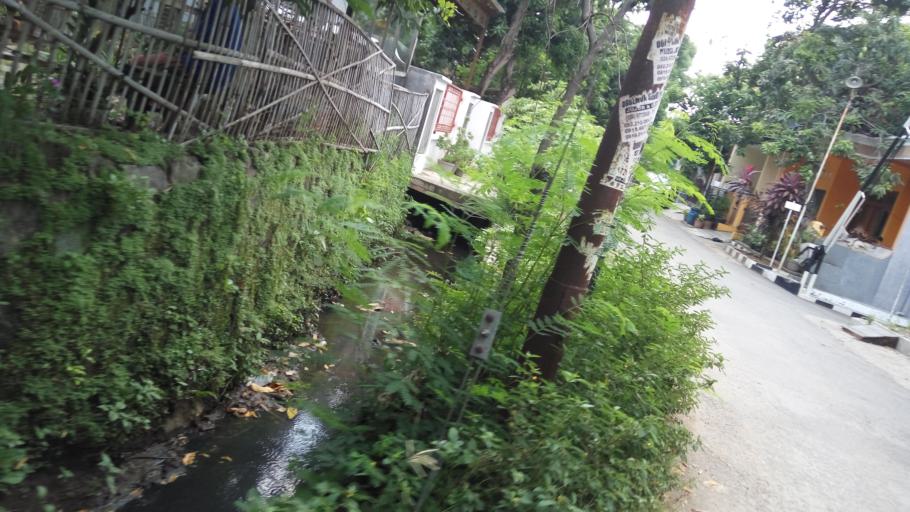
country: ID
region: Central Java
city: Mranggen
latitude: -7.0371
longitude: 110.4704
